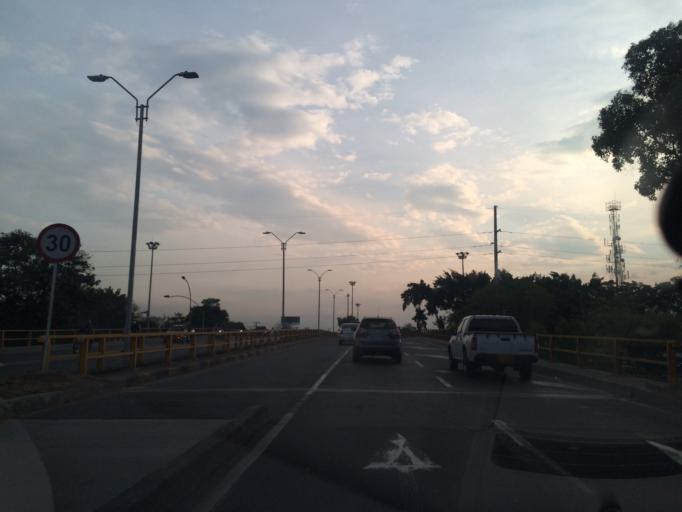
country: CO
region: Valle del Cauca
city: Cali
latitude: 3.4852
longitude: -76.4956
